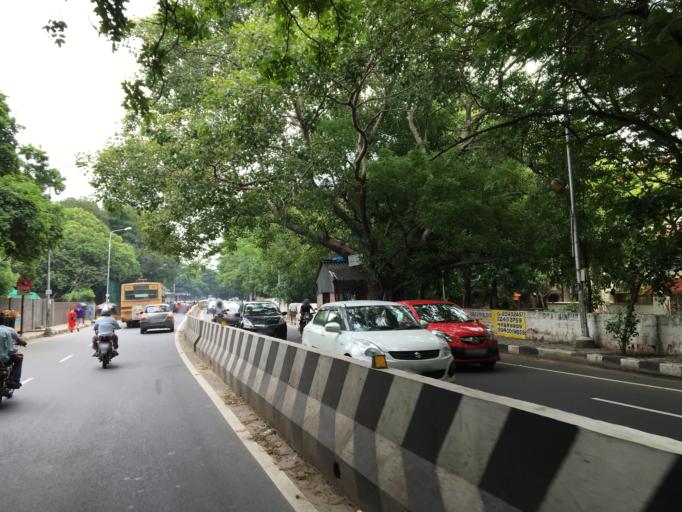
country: IN
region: Tamil Nadu
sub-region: Kancheepuram
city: Alandur
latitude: 12.9963
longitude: 80.2166
